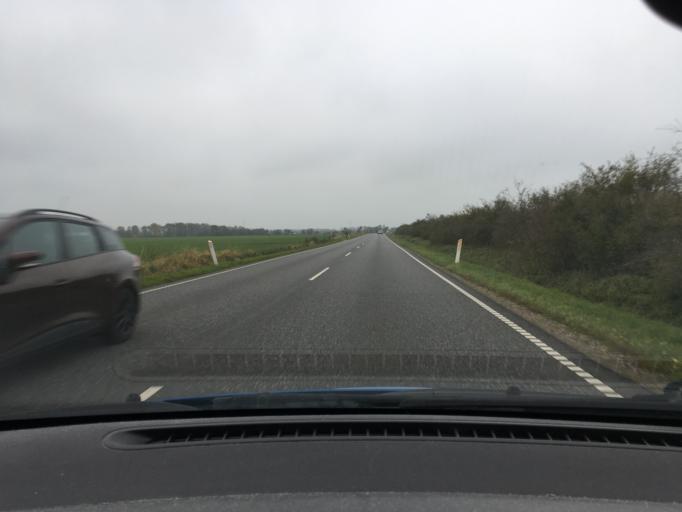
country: DK
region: South Denmark
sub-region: Tonder Kommune
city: Toftlund
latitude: 55.0545
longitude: 9.1069
